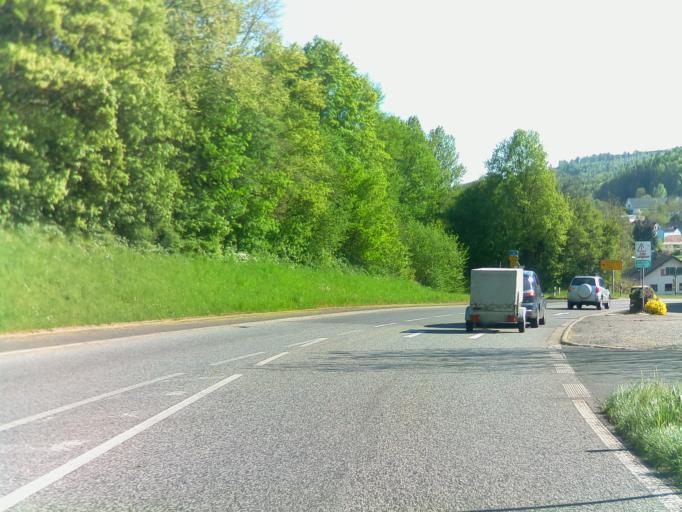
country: DE
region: Hesse
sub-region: Regierungsbezirk Darmstadt
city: Birstein
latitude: 50.3157
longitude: 9.2921
